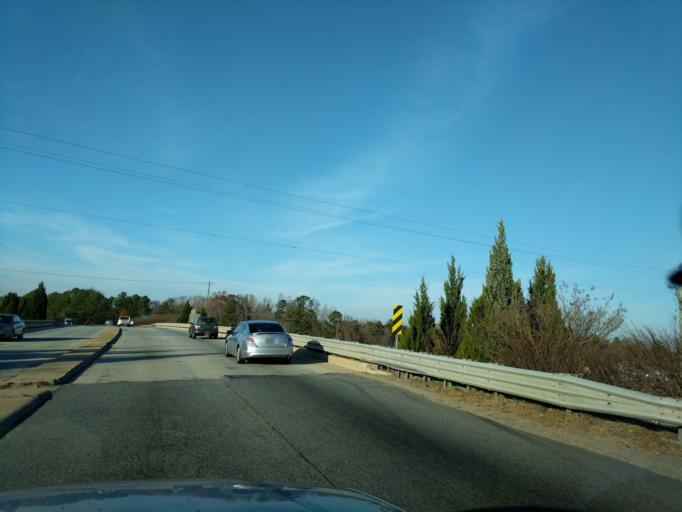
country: US
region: South Carolina
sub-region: Spartanburg County
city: Valley Falls
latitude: 34.9933
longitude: -81.9465
